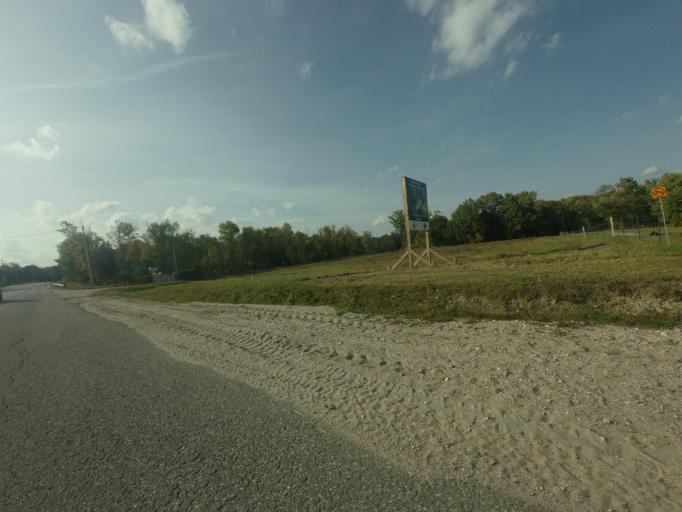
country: CA
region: Quebec
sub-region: Outaouais
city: Maniwaki
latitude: 46.3645
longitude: -75.9900
